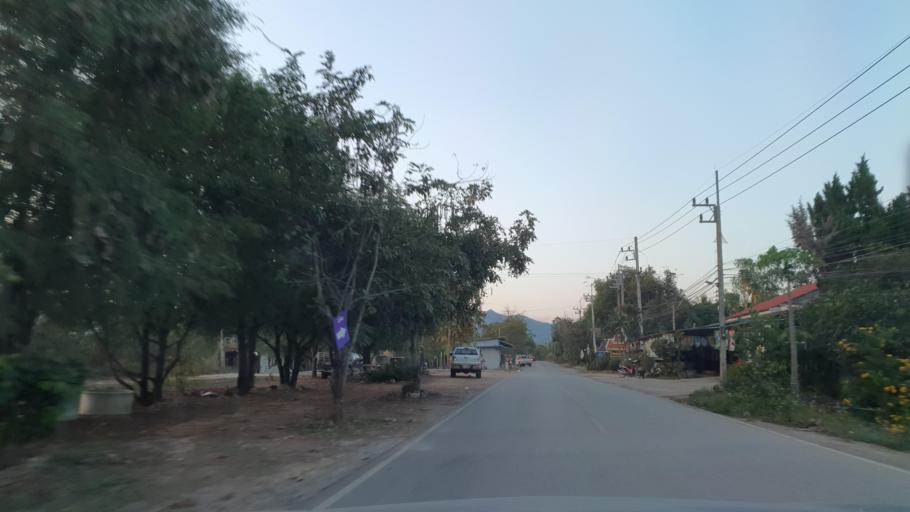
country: TH
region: Chiang Mai
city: Mae Wang
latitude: 18.6350
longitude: 98.8007
